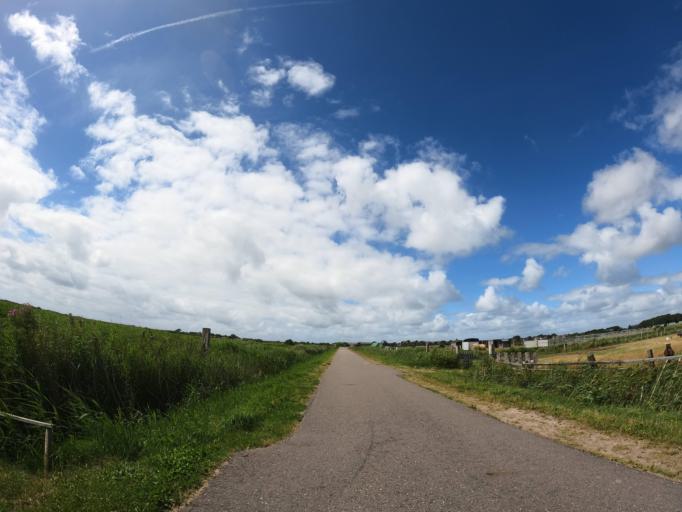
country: DE
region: Schleswig-Holstein
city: Tinnum
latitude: 54.8903
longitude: 8.3412
